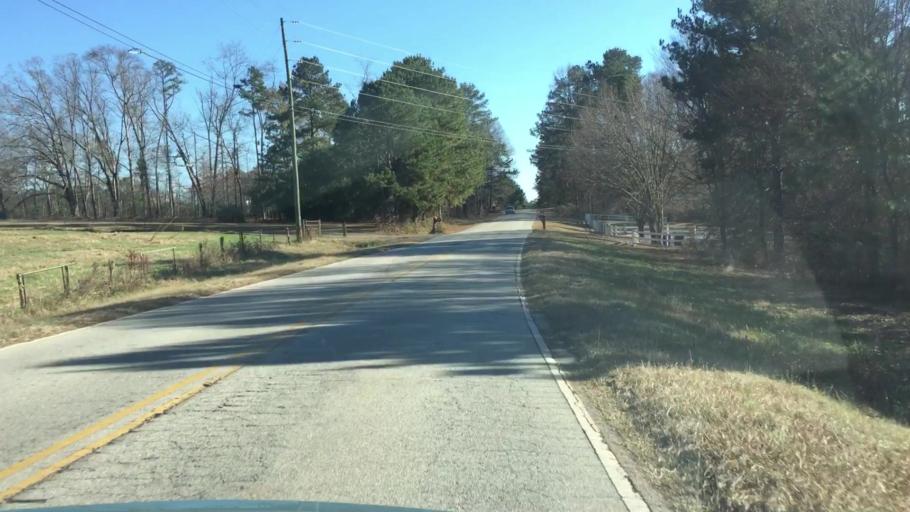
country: US
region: Georgia
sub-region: Henry County
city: McDonough
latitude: 33.5002
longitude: -84.0741
